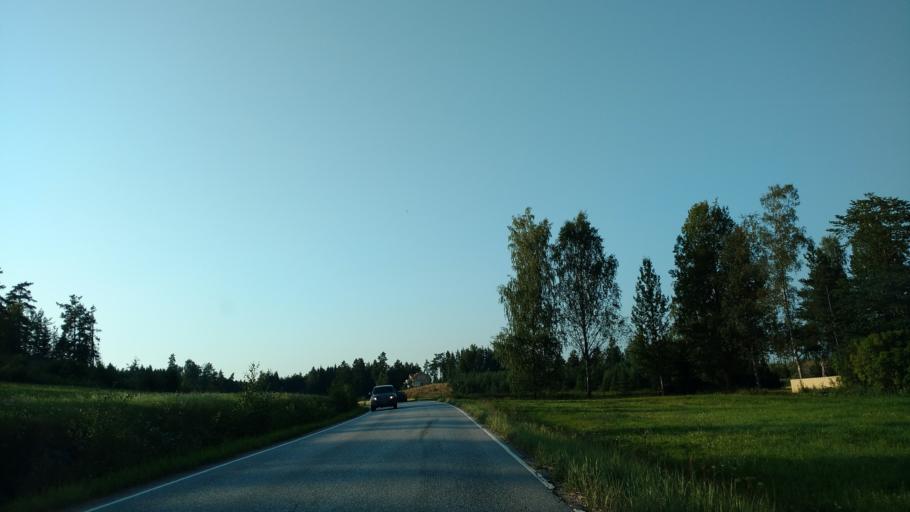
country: FI
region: Varsinais-Suomi
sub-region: Aboland-Turunmaa
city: Dragsfjaerd
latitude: 60.0557
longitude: 22.4540
